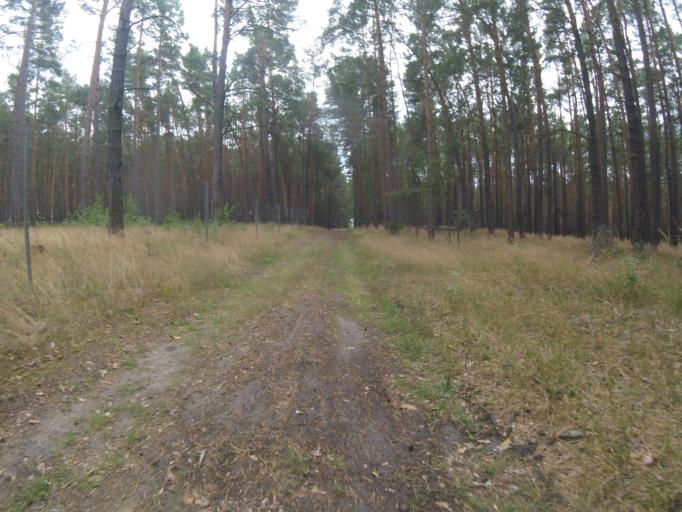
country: DE
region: Brandenburg
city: Bestensee
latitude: 52.2689
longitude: 13.7144
